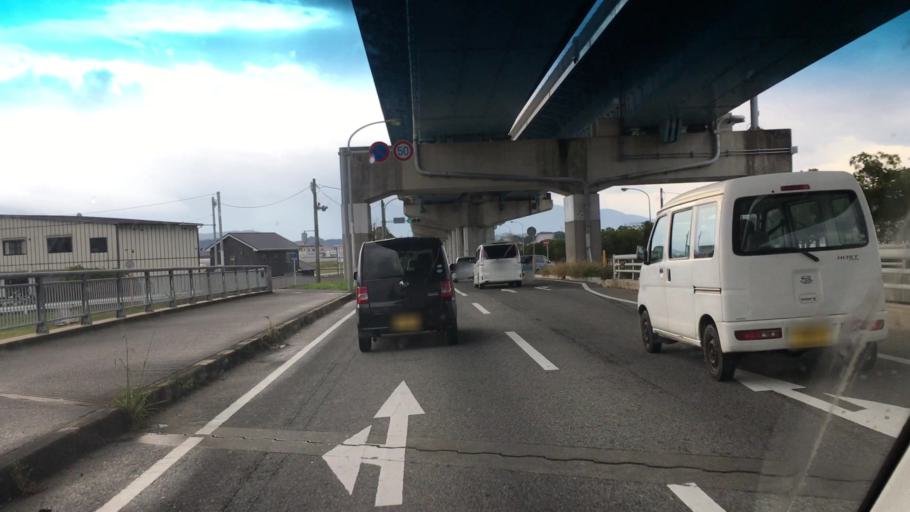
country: JP
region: Fukuoka
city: Maebaru-chuo
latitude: 33.5607
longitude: 130.2326
